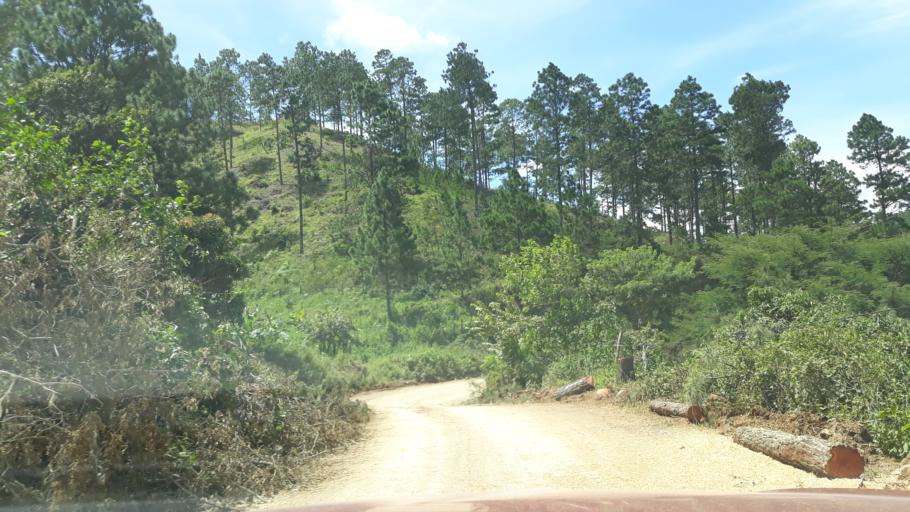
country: HN
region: El Paraiso
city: Santa Cruz
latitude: 13.7538
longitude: -86.6582
